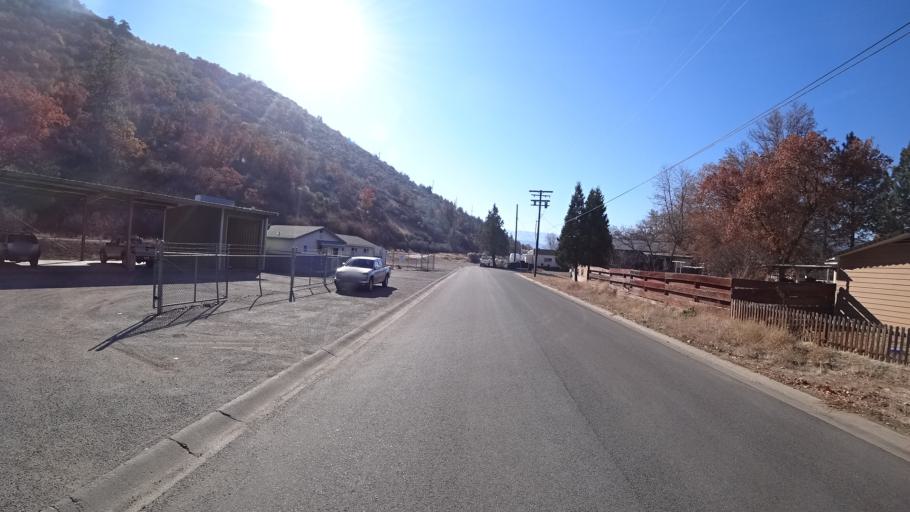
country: US
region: California
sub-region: Siskiyou County
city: Yreka
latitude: 41.7266
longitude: -122.6340
